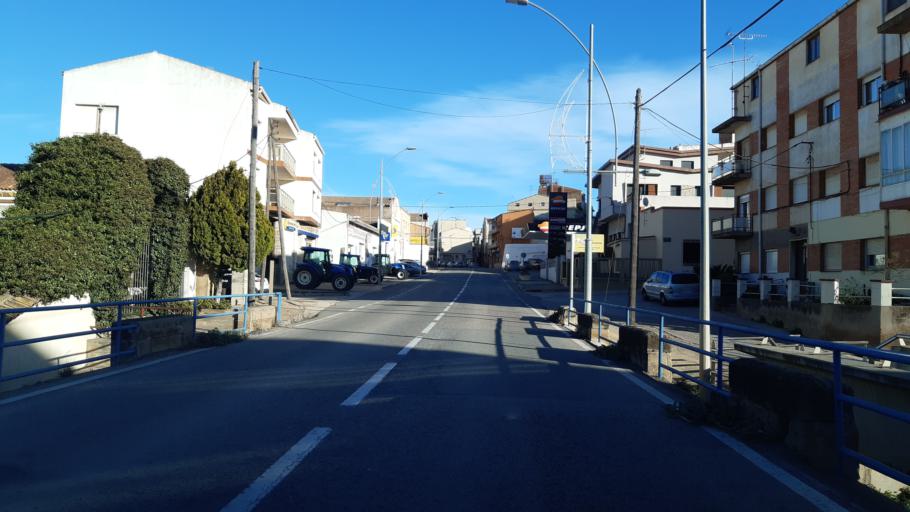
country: ES
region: Catalonia
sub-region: Provincia de Tarragona
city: Gandesa
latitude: 41.0539
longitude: 0.4350
